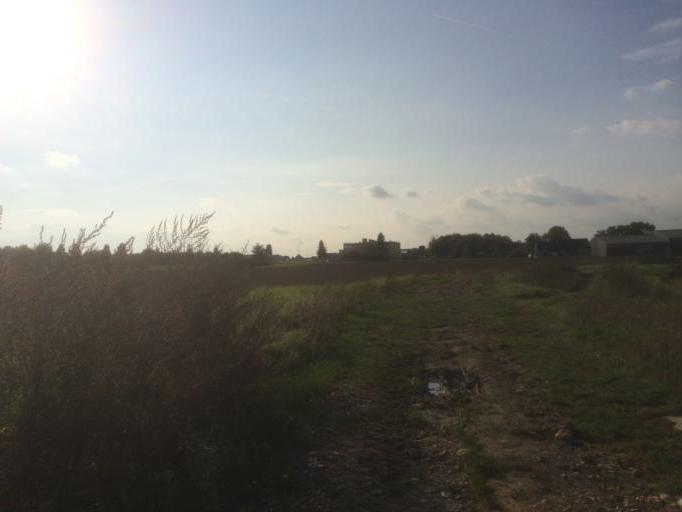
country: FR
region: Ile-de-France
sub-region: Departement des Yvelines
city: Les Loges-en-Josas
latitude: 48.7504
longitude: 2.1244
